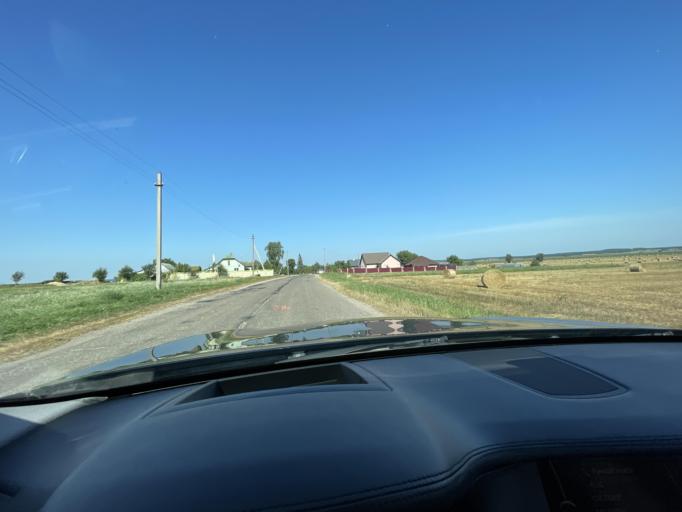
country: BY
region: Grodnenskaya
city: Hrodna
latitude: 53.7116
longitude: 23.9809
